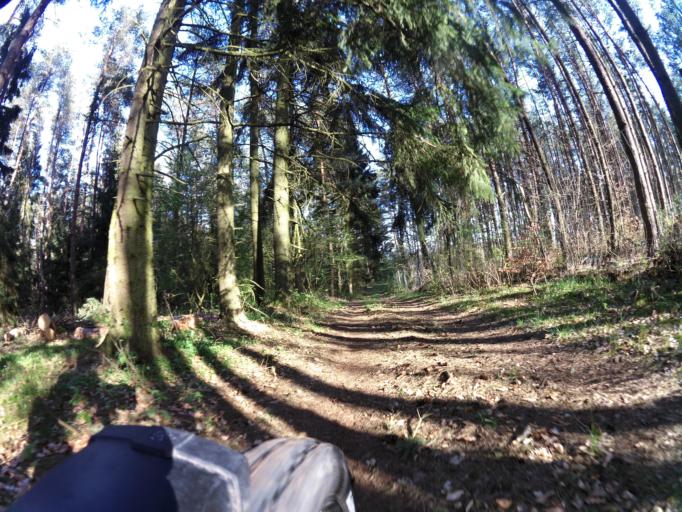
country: PL
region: West Pomeranian Voivodeship
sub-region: Powiat lobeski
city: Lobez
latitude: 53.7504
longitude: 15.6086
